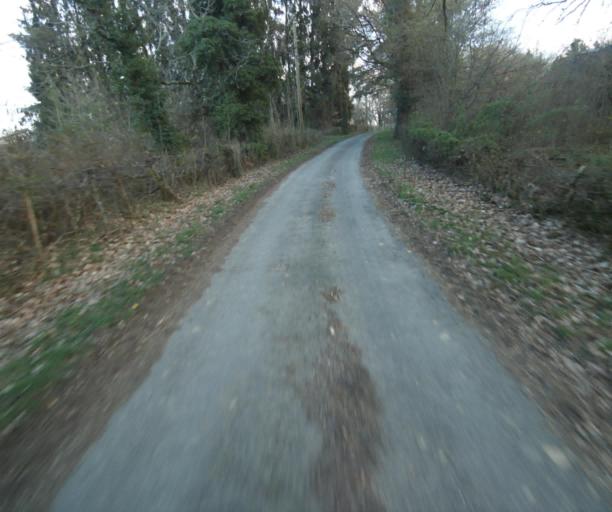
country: FR
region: Limousin
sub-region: Departement de la Correze
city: Uzerche
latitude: 45.3713
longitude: 1.5855
